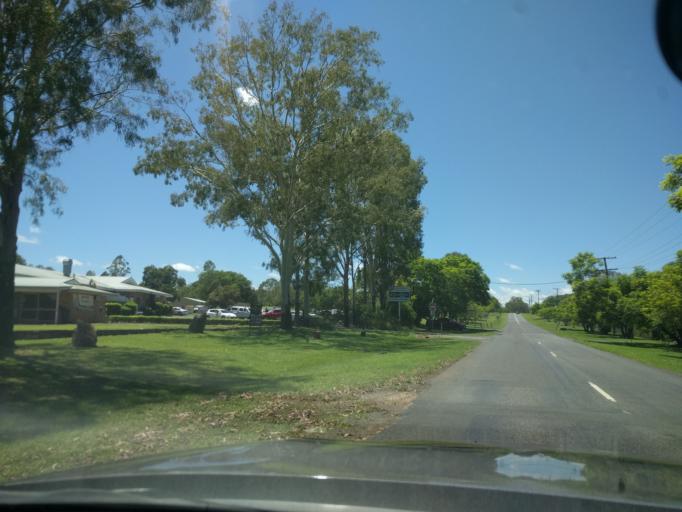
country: AU
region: Queensland
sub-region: Logan
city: Cedar Vale
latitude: -27.9983
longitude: 153.0007
